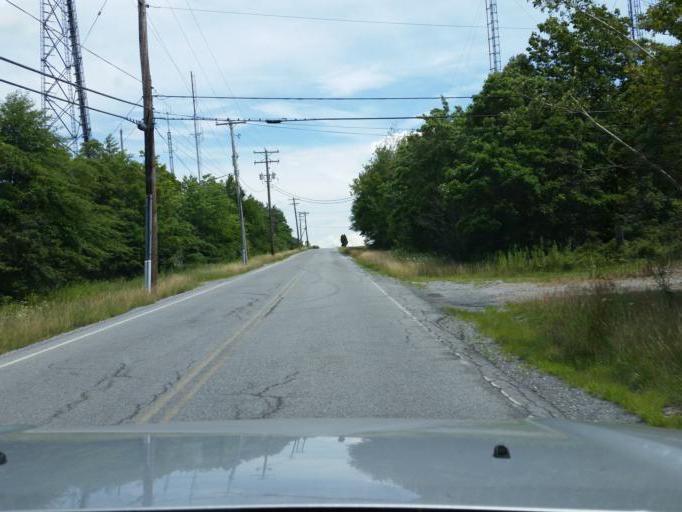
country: US
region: Pennsylvania
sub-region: Blair County
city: Altoona
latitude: 40.5675
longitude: -78.4432
